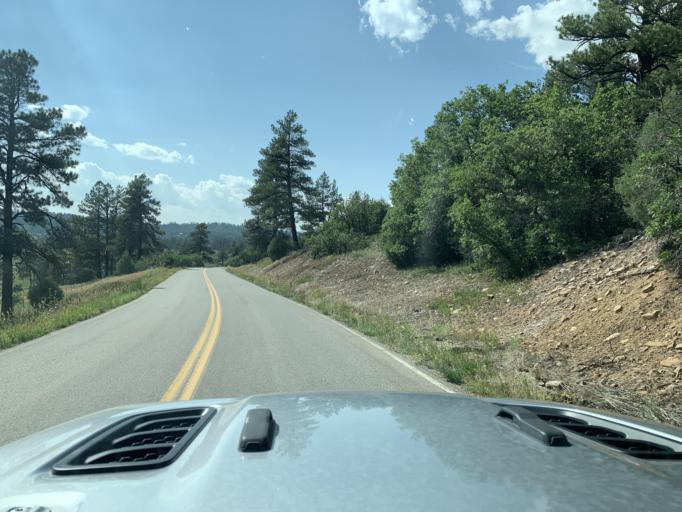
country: US
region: Colorado
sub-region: Archuleta County
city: Pagosa Springs
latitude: 37.2420
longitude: -107.0282
